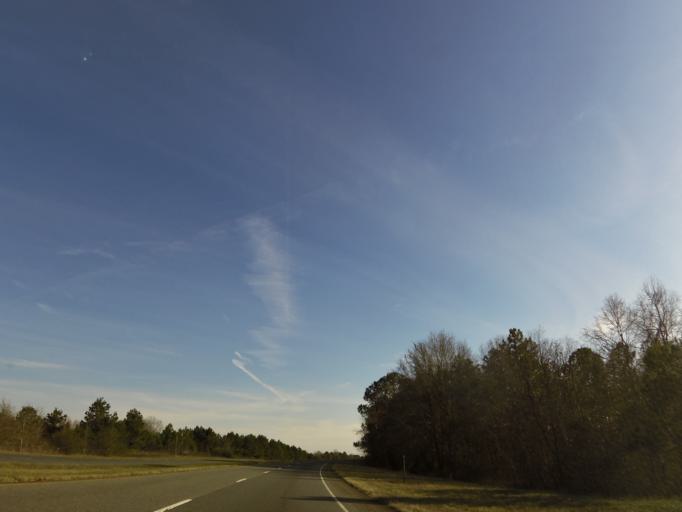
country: US
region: Georgia
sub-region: Stewart County
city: Richland
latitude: 32.1320
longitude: -84.6835
